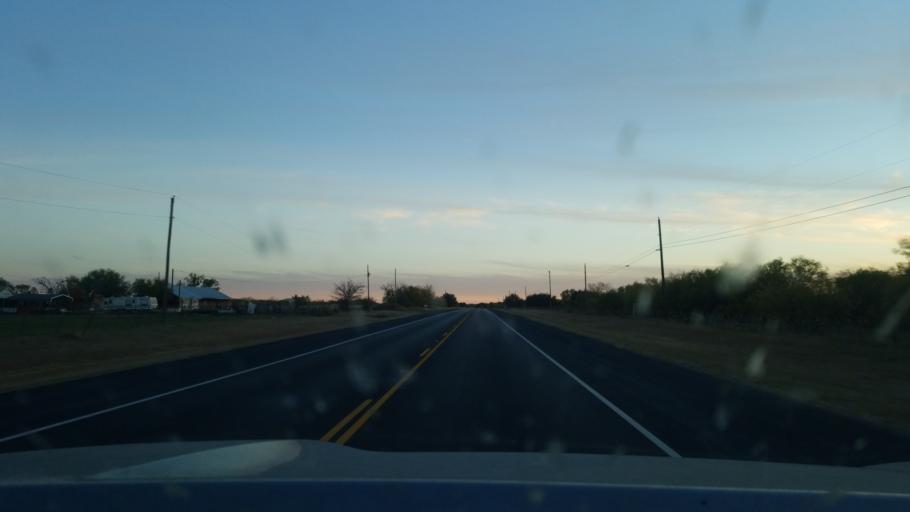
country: US
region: Texas
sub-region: Stephens County
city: Breckenridge
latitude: 32.6319
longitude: -98.9028
